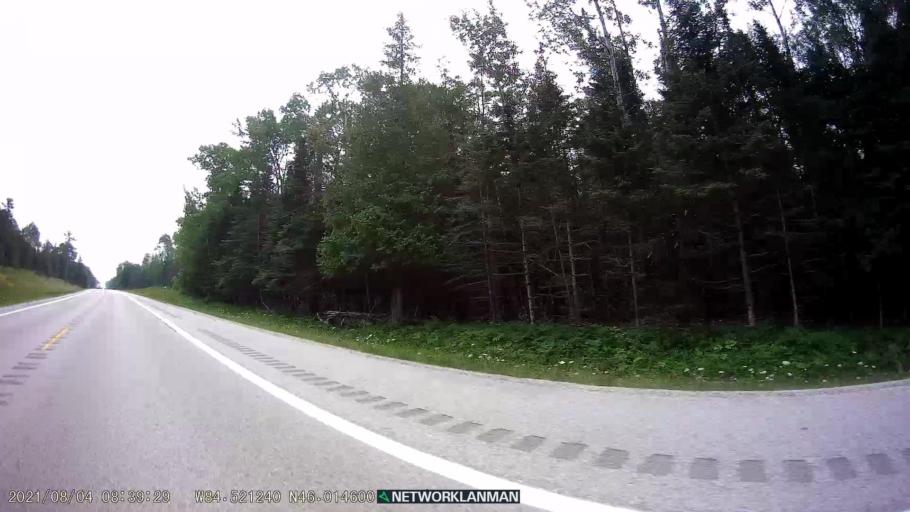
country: US
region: Michigan
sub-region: Mackinac County
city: Saint Ignace
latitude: 46.0145
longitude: -84.5189
